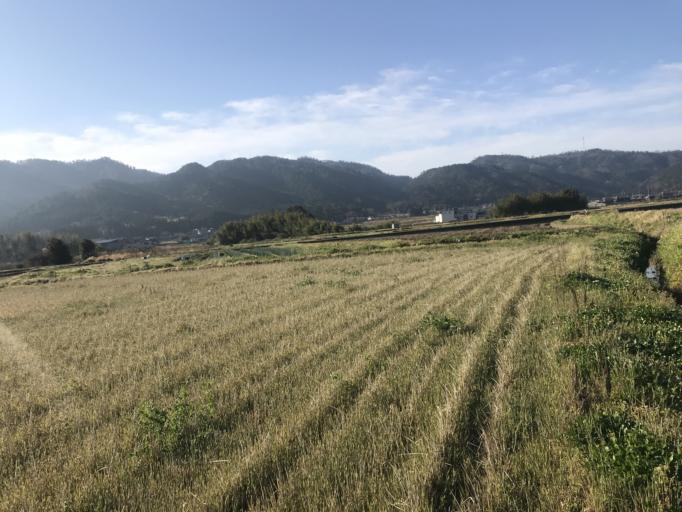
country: JP
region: Kyoto
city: Kameoka
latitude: 34.9901
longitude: 135.5435
